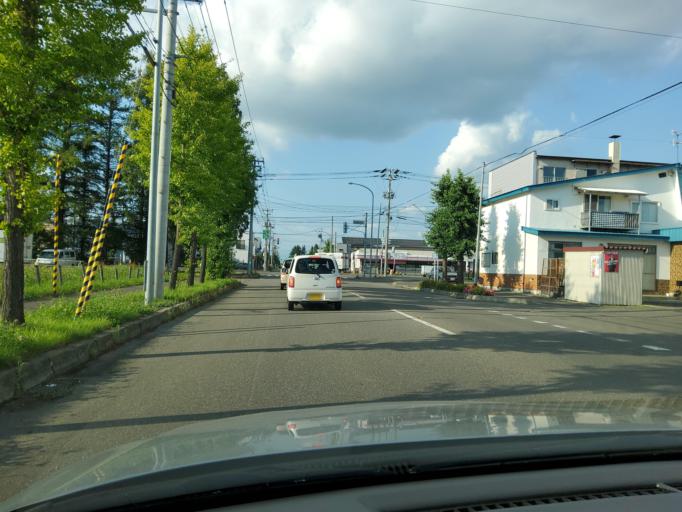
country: JP
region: Hokkaido
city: Obihiro
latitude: 42.9091
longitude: 143.1729
